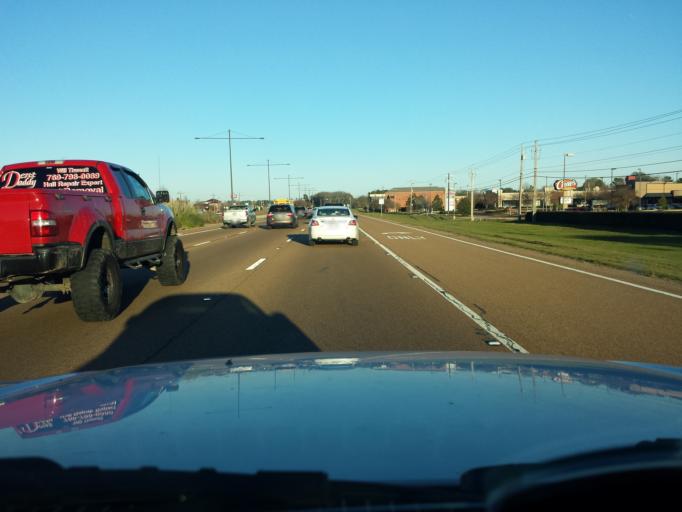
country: US
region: Mississippi
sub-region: Rankin County
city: Flowood
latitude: 32.3316
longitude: -90.1072
